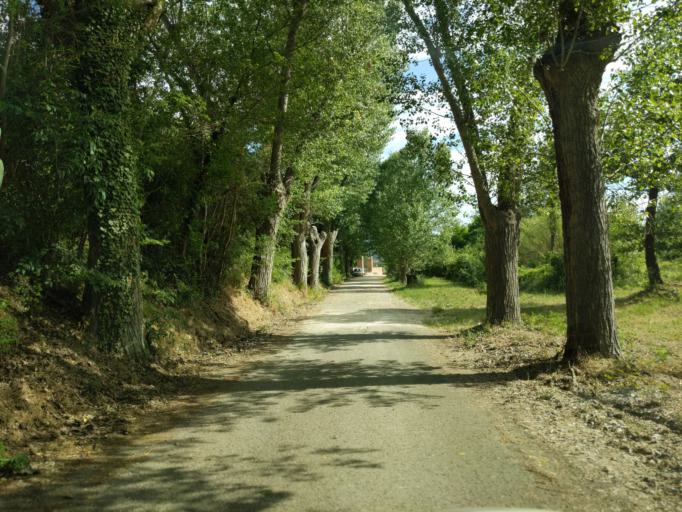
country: IT
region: The Marches
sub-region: Provincia di Pesaro e Urbino
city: Gradara
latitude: 43.9426
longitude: 12.7828
